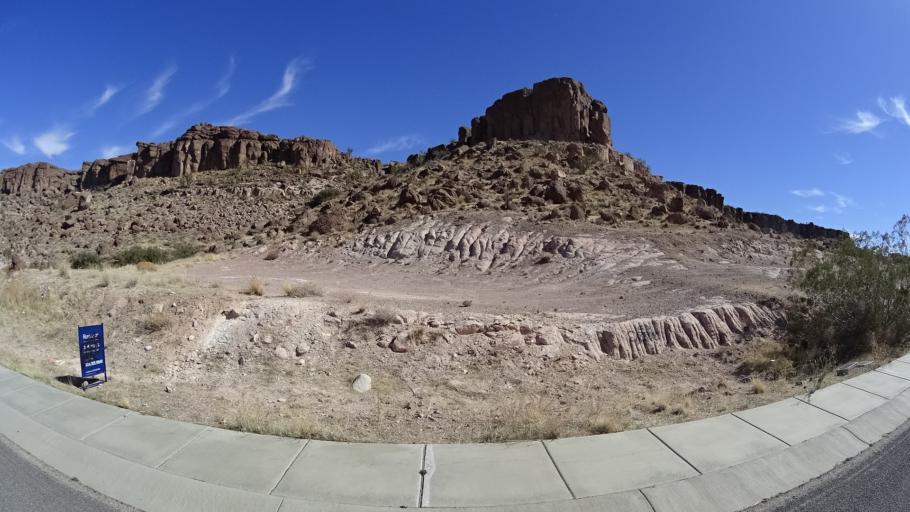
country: US
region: Arizona
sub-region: Mohave County
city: Kingman
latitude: 35.2069
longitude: -114.0552
